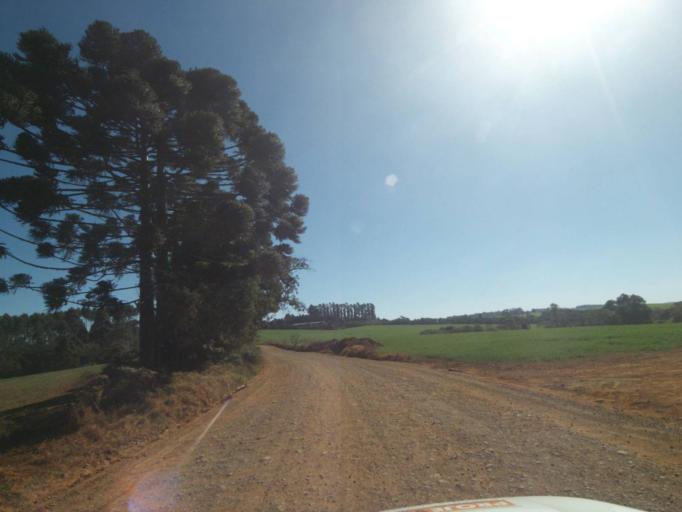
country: BR
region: Parana
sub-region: Reserva
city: Reserva
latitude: -24.6257
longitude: -50.6285
